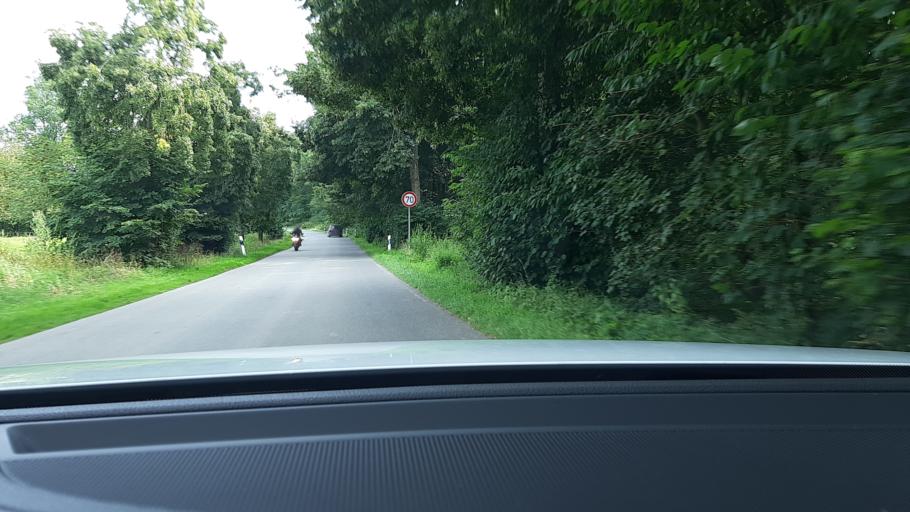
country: DE
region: Schleswig-Holstein
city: Rehhorst
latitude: 53.8574
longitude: 10.4662
